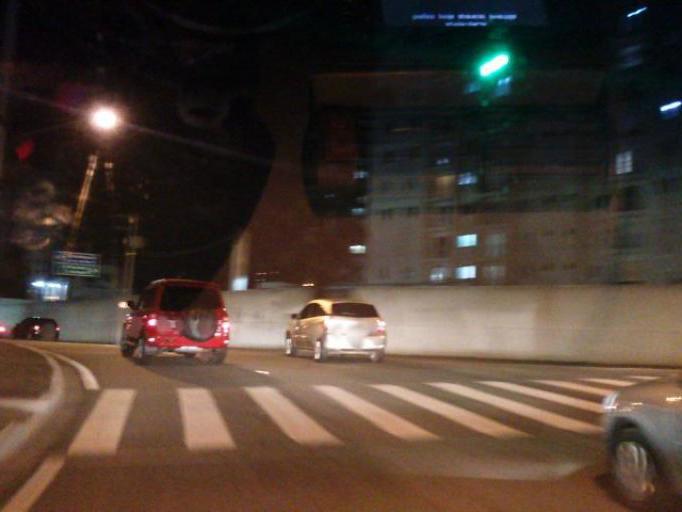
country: BR
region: Sao Paulo
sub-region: Sao Jose Dos Campos
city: Sao Jose dos Campos
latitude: -23.1799
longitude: -45.8699
